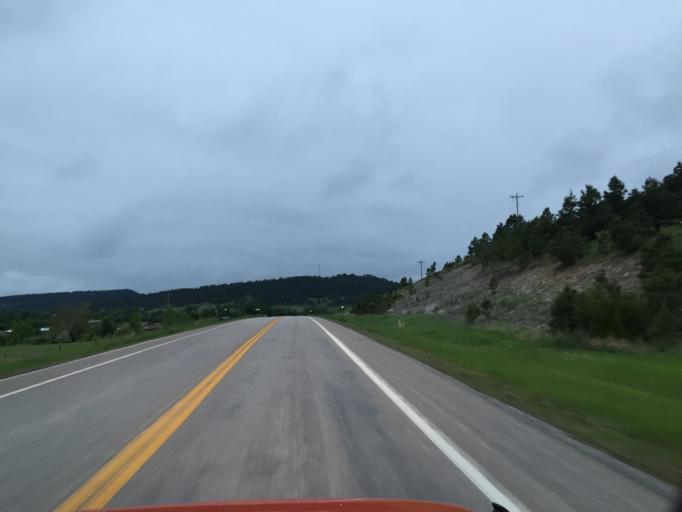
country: US
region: South Dakota
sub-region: Pennington County
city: Colonial Pine Hills
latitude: 43.8338
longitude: -103.2195
